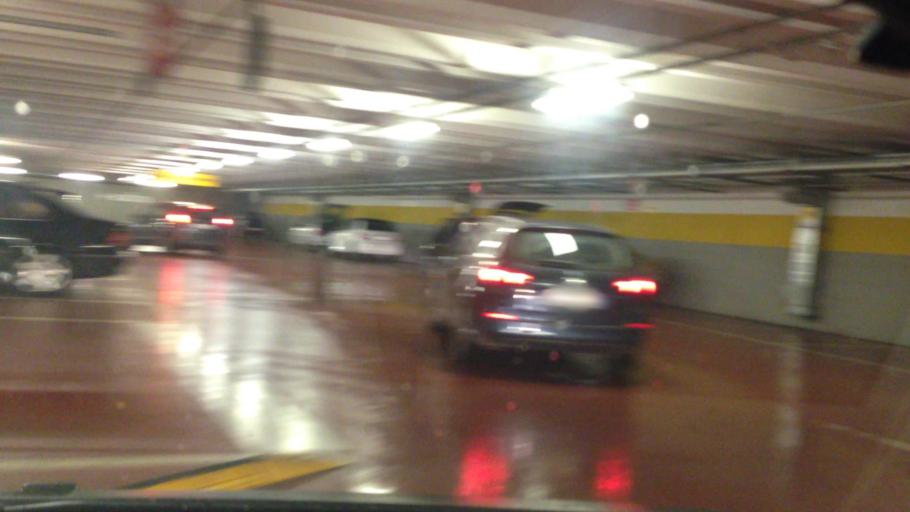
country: IT
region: Piedmont
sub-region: Provincia di Asti
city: Asti
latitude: 44.9158
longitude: 8.2232
